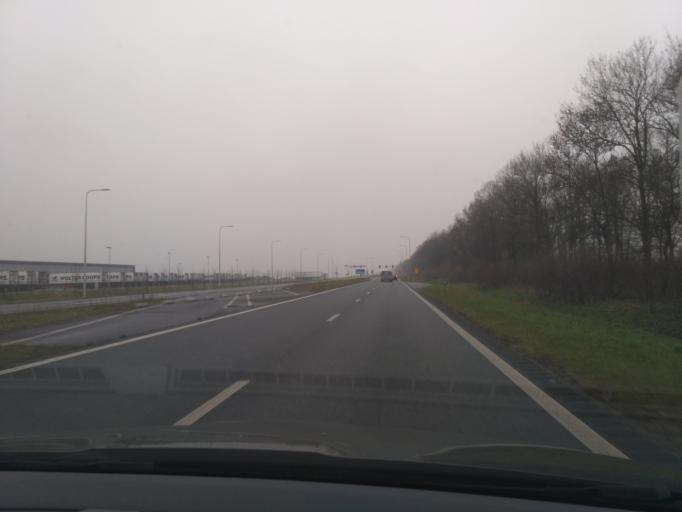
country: NL
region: Flevoland
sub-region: Gemeente Zeewolde
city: Zeewolde
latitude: 52.3591
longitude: 5.5193
